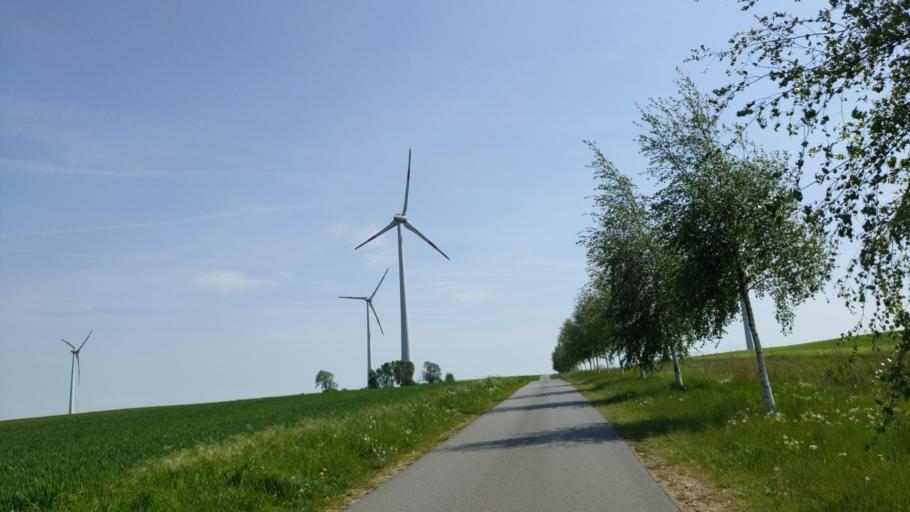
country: DE
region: Mecklenburg-Vorpommern
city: Selmsdorf
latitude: 53.8784
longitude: 10.8952
